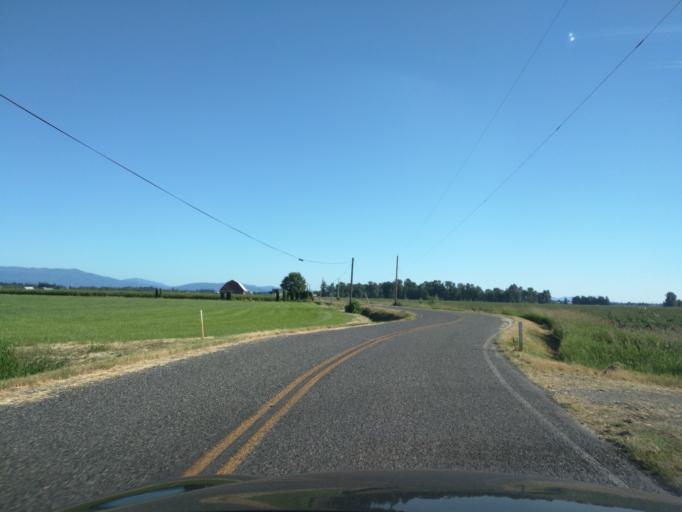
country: US
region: Washington
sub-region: Whatcom County
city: Lynden
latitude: 48.9933
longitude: -122.4410
